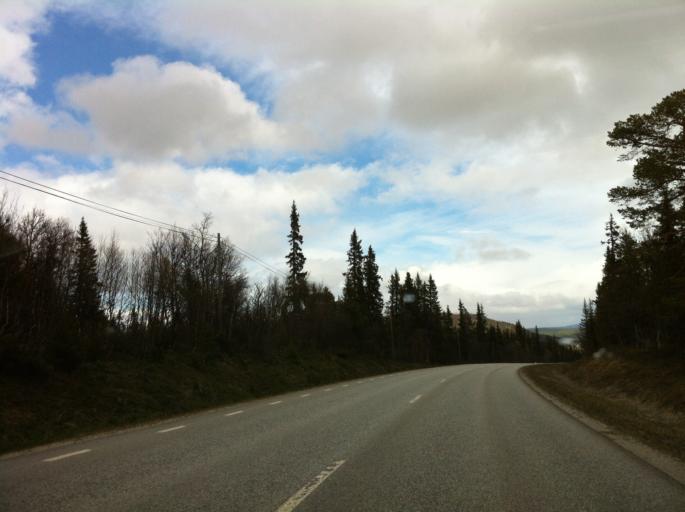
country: NO
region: Hedmark
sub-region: Engerdal
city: Engerdal
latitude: 62.5373
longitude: 12.4150
